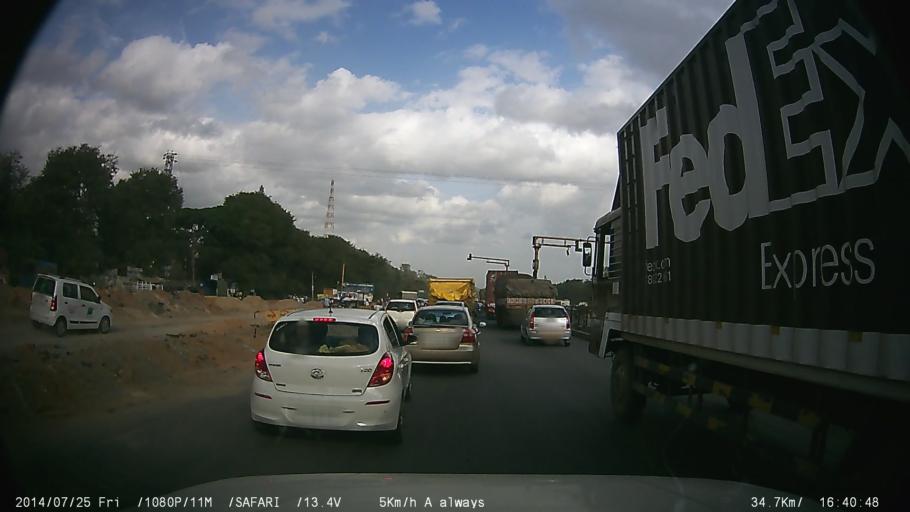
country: IN
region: Tamil Nadu
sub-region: Krishnagiri
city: Hosur
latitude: 12.7628
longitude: 77.7939
